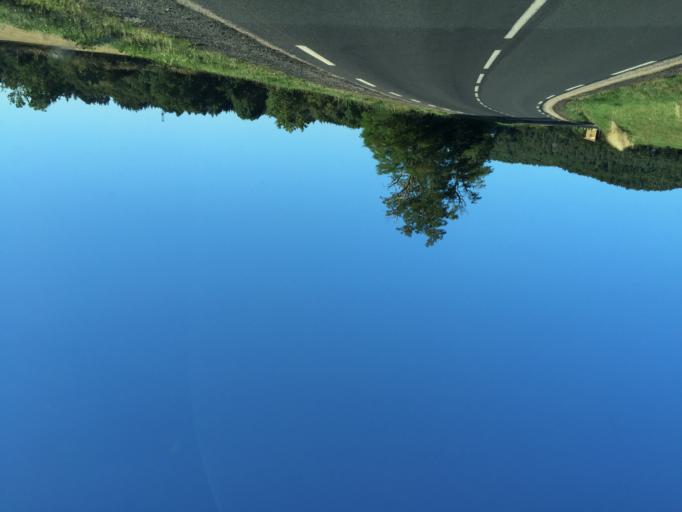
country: FR
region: Auvergne
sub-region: Departement de la Haute-Loire
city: Bains
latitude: 44.9887
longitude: 3.6969
